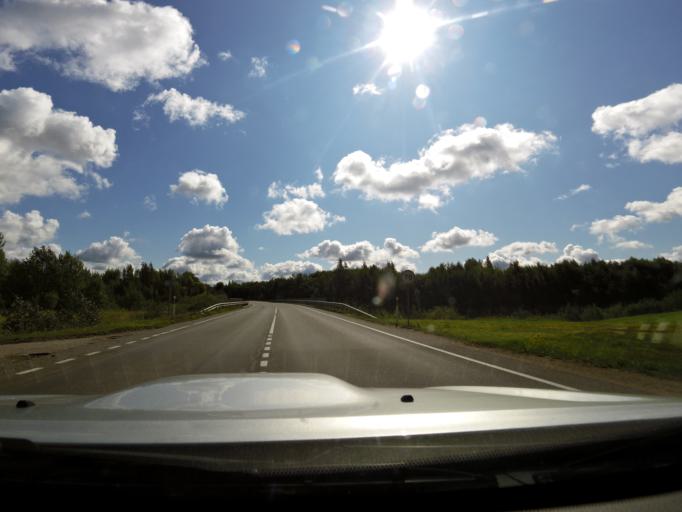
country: LT
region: Utenos apskritis
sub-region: Utena
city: Utena
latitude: 55.4857
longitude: 25.6380
